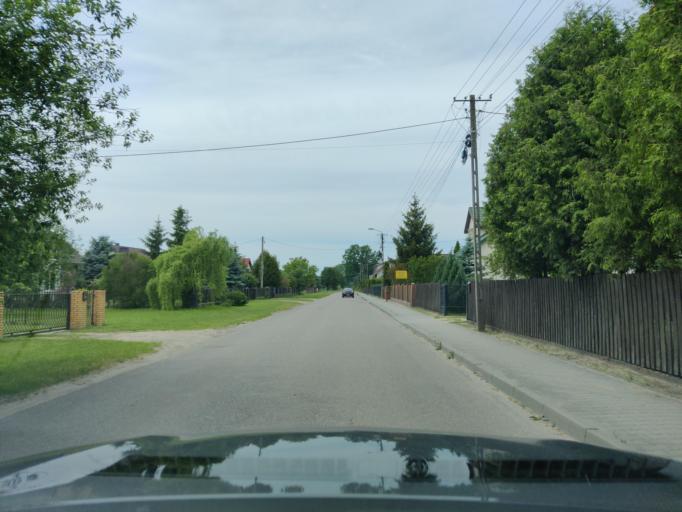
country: PL
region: Masovian Voivodeship
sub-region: Powiat wyszkowski
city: Rzasnik
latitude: 52.6989
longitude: 21.4128
